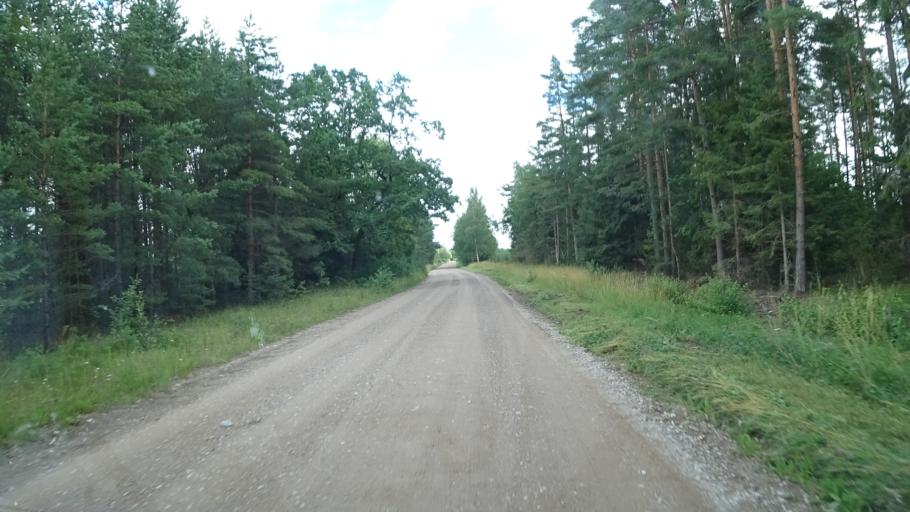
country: LV
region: Pavilostas
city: Pavilosta
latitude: 56.7488
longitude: 21.2517
